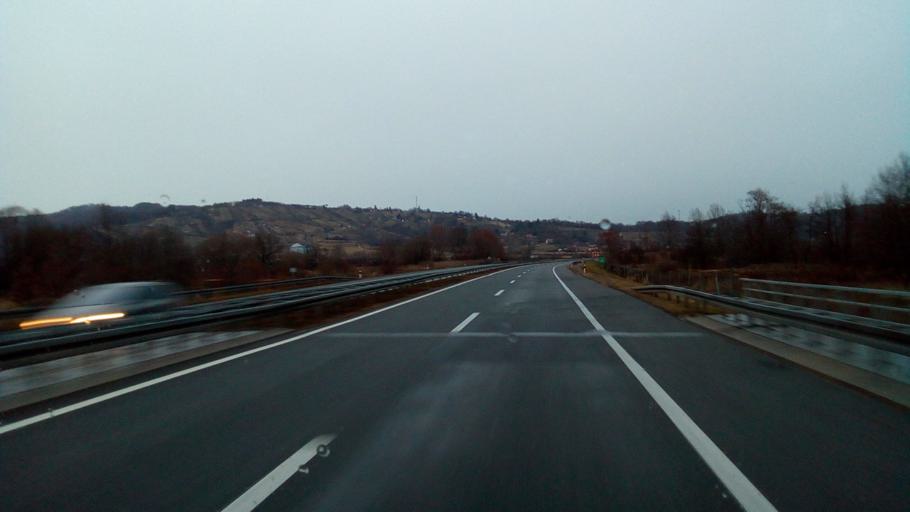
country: HR
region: Varazdinska
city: Ljubescica
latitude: 46.1845
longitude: 16.3986
